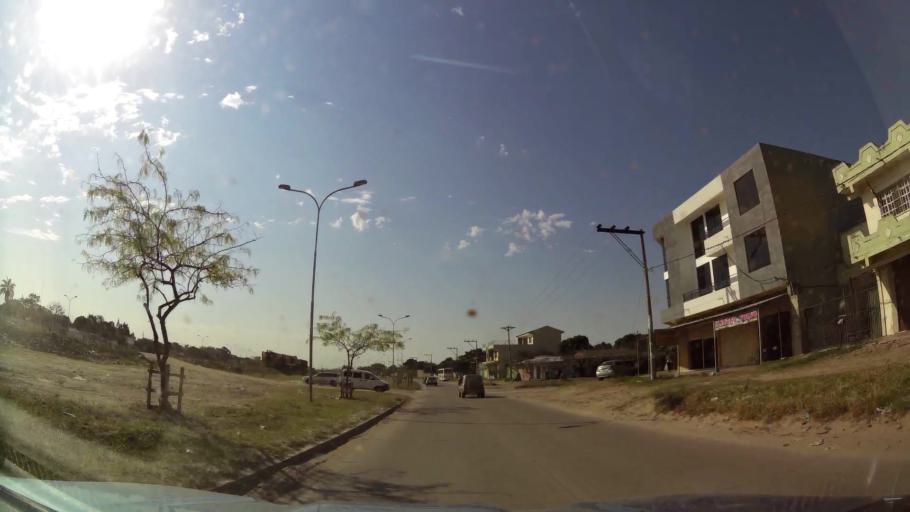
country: BO
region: Santa Cruz
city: Santa Cruz de la Sierra
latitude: -17.8075
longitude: -63.1408
